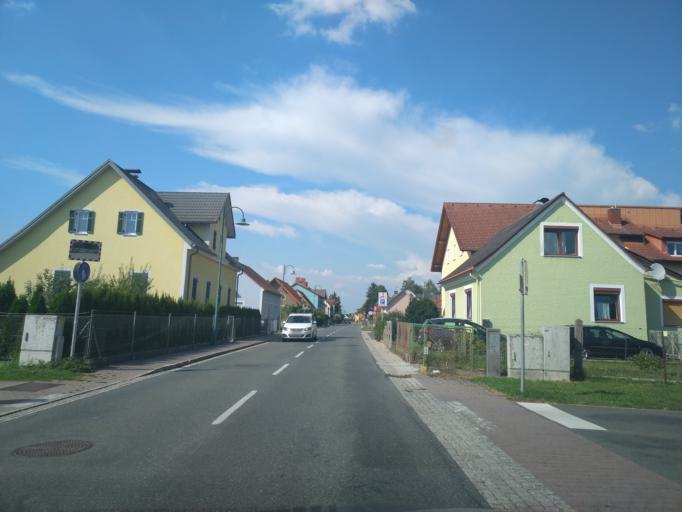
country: AT
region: Styria
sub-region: Politischer Bezirk Leibnitz
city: Kaindorf an der Sulm
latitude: 46.7902
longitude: 15.5384
